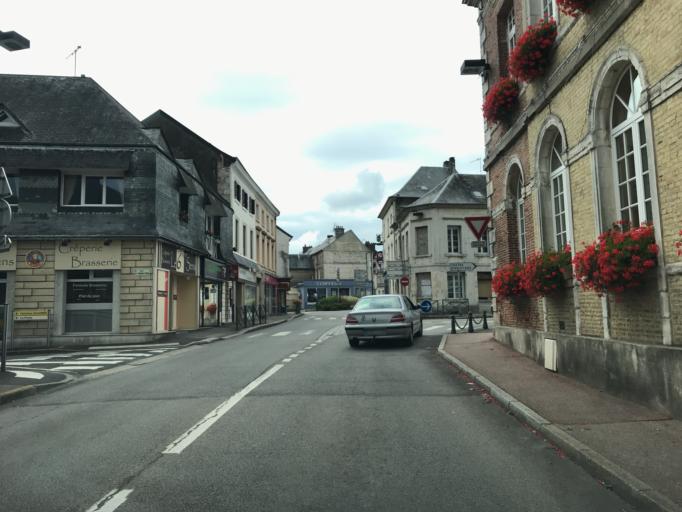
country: FR
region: Haute-Normandie
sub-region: Departement de la Seine-Maritime
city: Goderville
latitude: 49.6455
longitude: 0.3681
